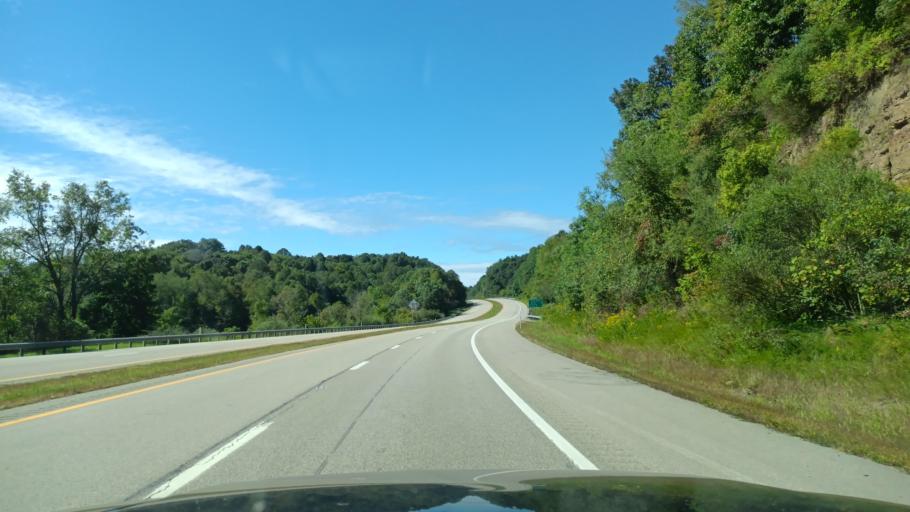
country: US
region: West Virginia
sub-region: Harrison County
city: Salem
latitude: 39.2898
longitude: -80.5380
